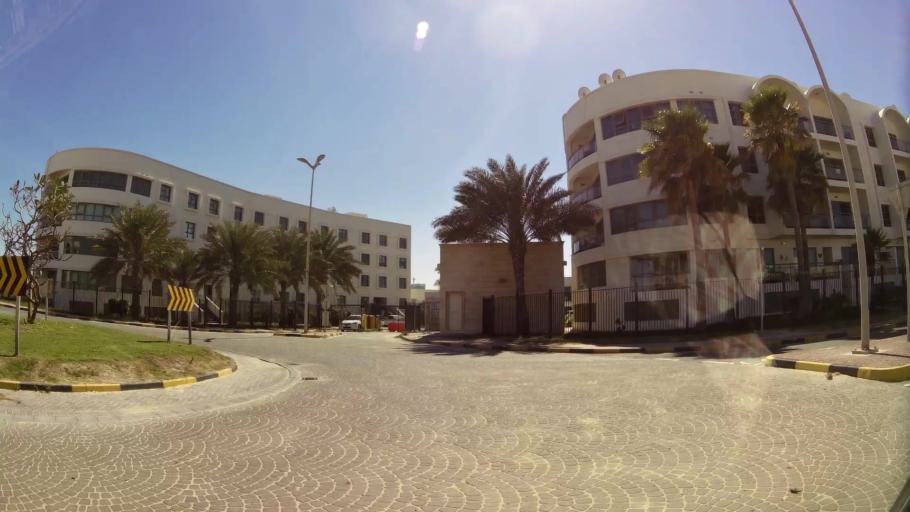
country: BH
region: Muharraq
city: Al Hadd
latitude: 26.2994
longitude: 50.6659
